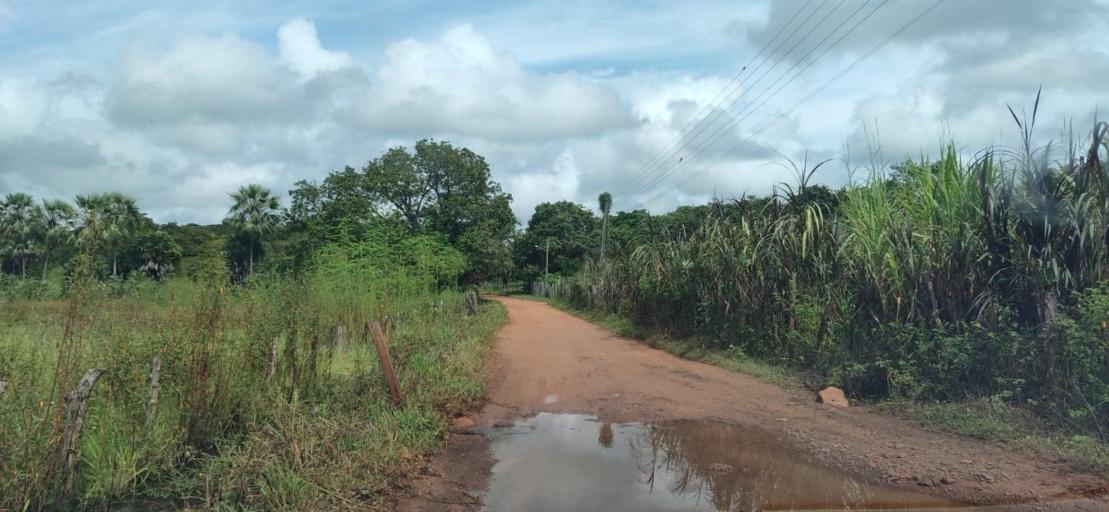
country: BR
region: Piaui
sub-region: Valenca Do Piaui
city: Valenca do Piaui
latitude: -6.1095
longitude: -41.8016
